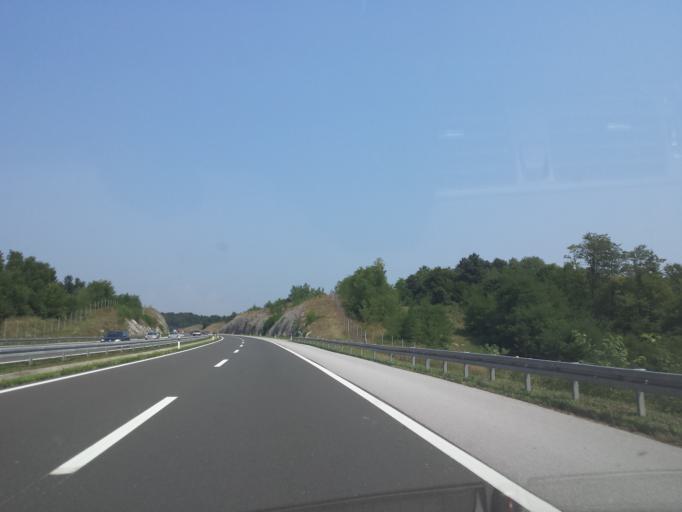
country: HR
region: Karlovacka
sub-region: Grad Ogulin
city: Ogulin
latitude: 45.3495
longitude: 15.2776
